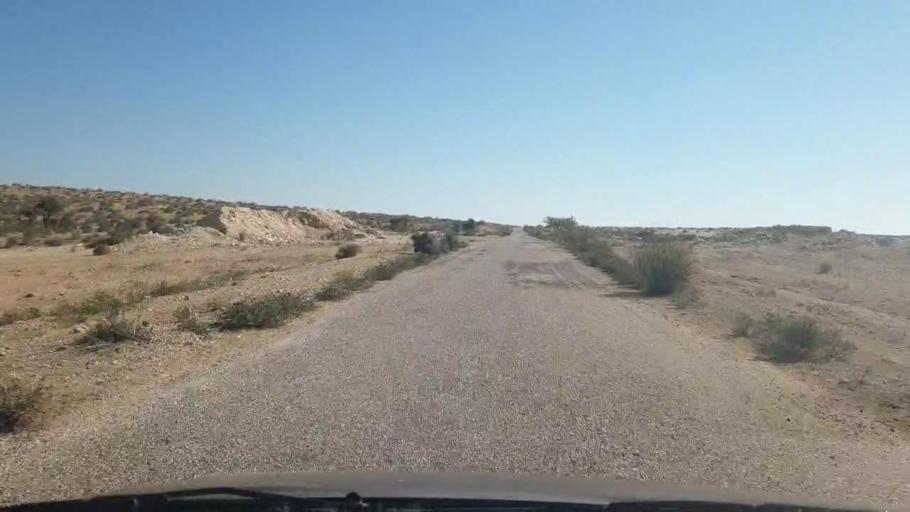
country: PK
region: Sindh
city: Bozdar
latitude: 27.0072
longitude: 68.8012
